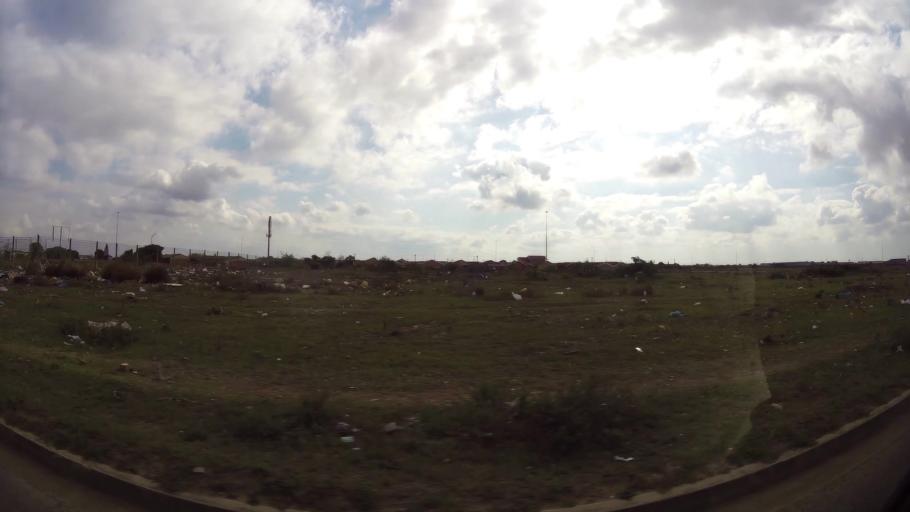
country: ZA
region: Eastern Cape
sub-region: Nelson Mandela Bay Metropolitan Municipality
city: Port Elizabeth
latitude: -33.8182
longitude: 25.5948
